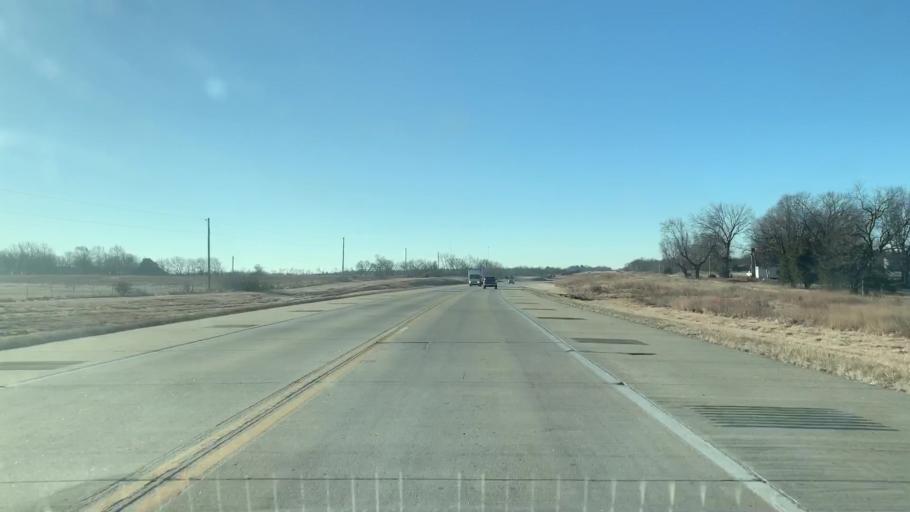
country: US
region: Kansas
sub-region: Crawford County
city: Arma
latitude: 37.5754
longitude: -94.7051
